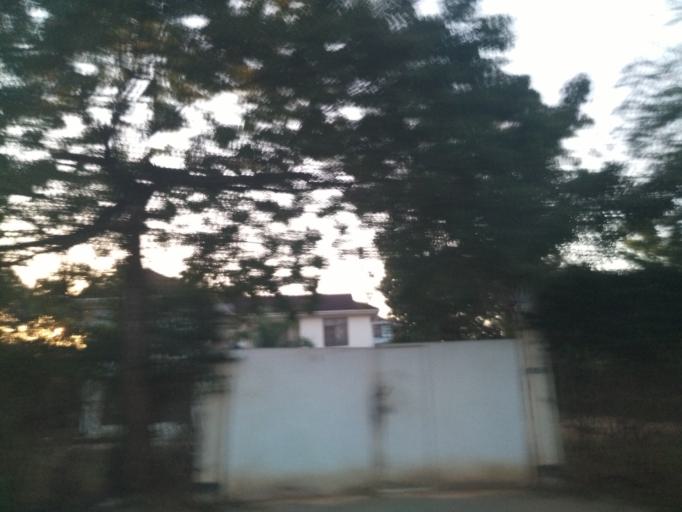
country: TZ
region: Dar es Salaam
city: Magomeni
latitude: -6.7757
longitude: 39.2514
